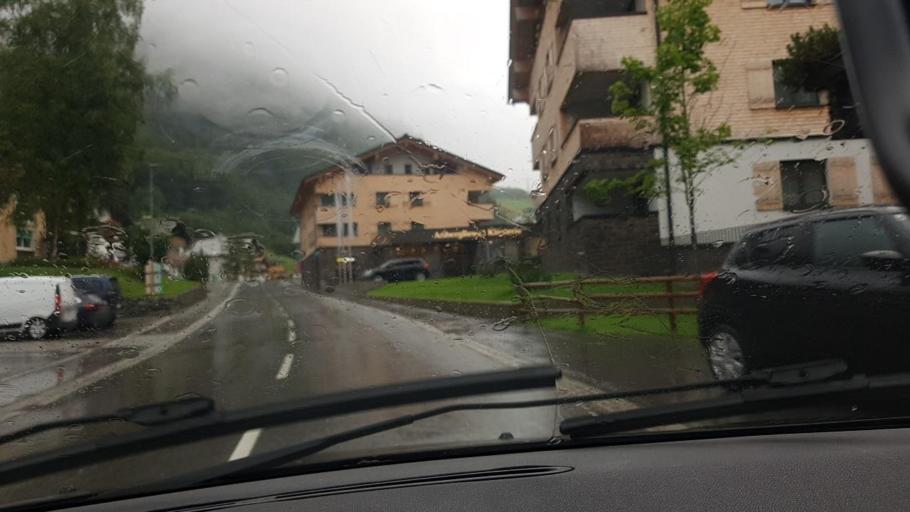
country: AT
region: Vorarlberg
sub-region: Politischer Bezirk Bludenz
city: Klosterle
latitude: 47.1312
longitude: 10.0920
